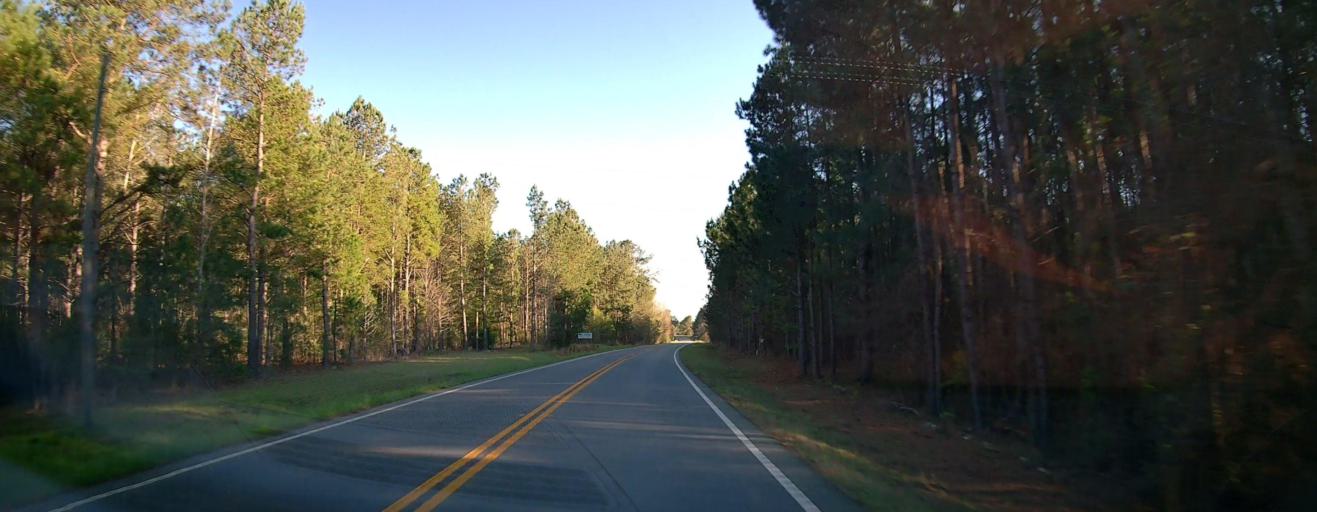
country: US
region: Georgia
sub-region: Pulaski County
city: Hawkinsville
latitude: 32.1965
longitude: -83.3712
